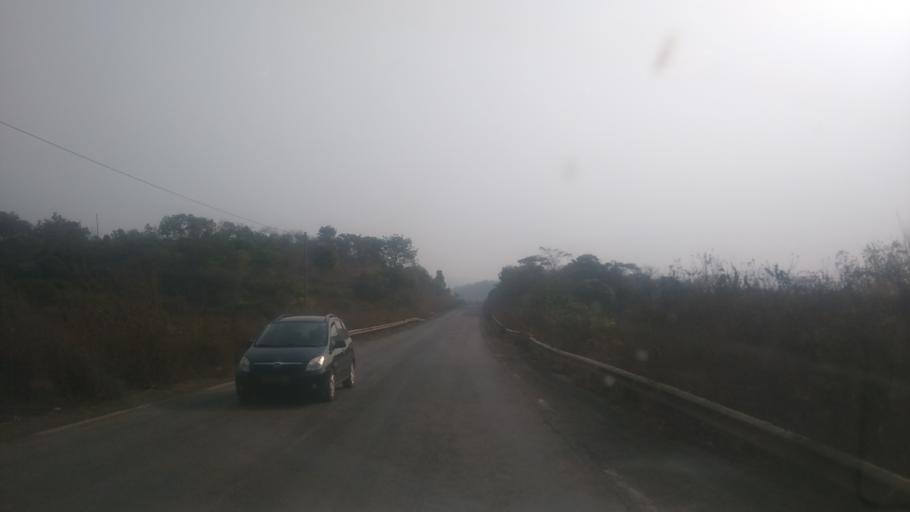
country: CM
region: West
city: Tonga
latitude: 5.0381
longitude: 10.7012
